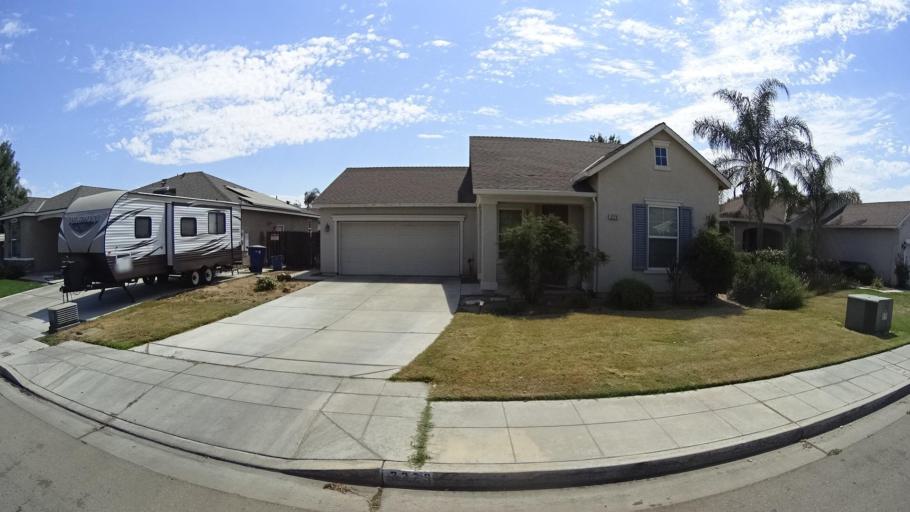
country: US
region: California
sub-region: Fresno County
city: Sunnyside
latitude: 36.7183
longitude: -119.7135
